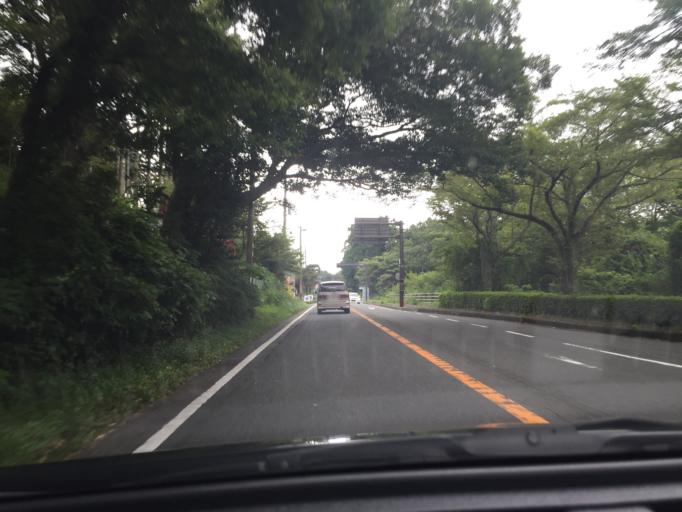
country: JP
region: Shizuoka
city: Ito
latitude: 34.9226
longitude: 139.1190
